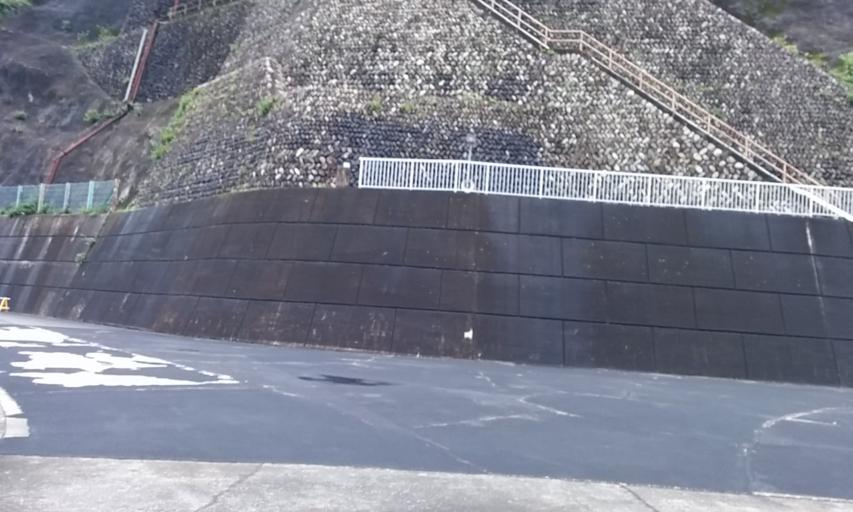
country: JP
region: Tokyo
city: Itsukaichi
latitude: 35.7912
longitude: 139.0510
